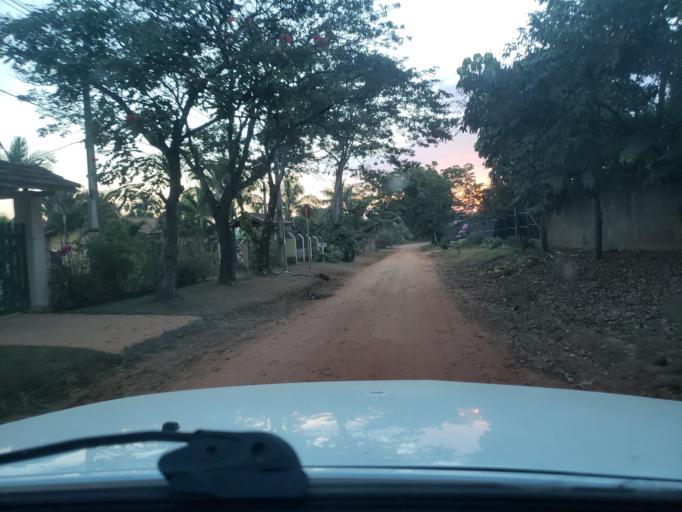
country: BR
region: Sao Paulo
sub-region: Mogi-Mirim
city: Mogi Mirim
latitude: -22.4948
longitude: -46.9808
